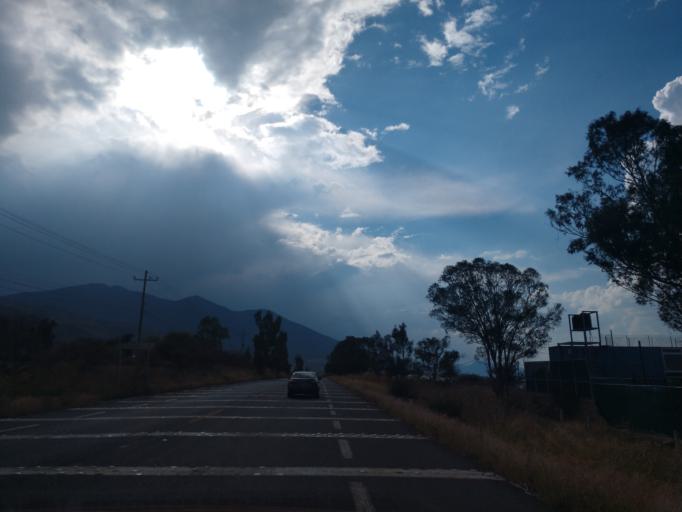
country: MX
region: Jalisco
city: San Juan Cosala
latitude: 20.1942
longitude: -103.2799
